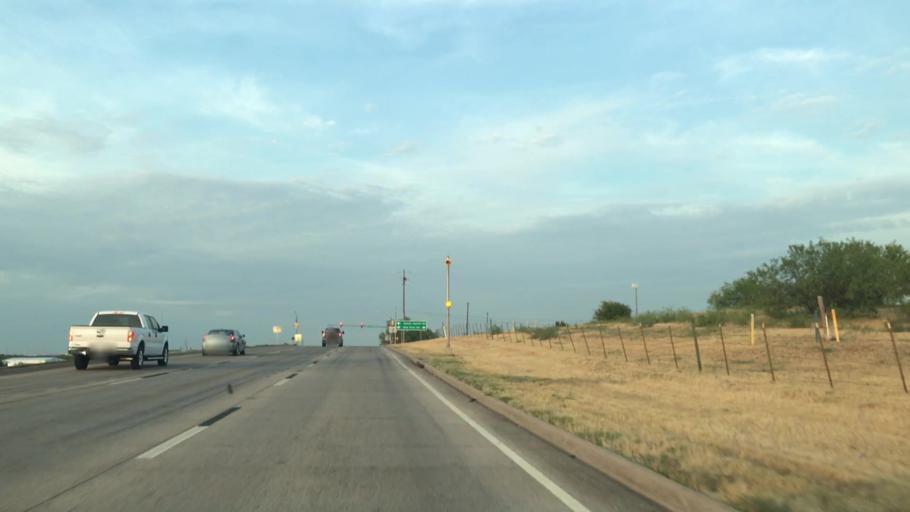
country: US
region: Texas
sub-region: Tarrant County
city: Keller
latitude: 32.9699
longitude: -97.2831
